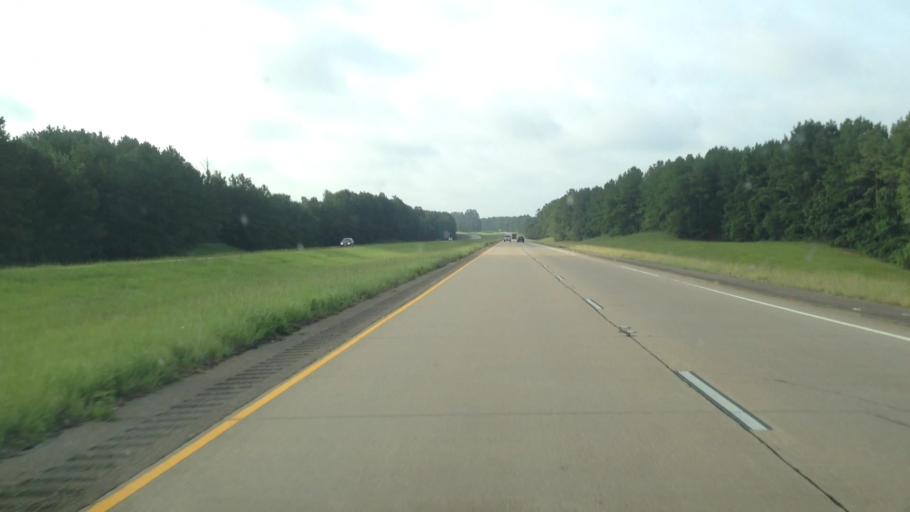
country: US
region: Louisiana
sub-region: Rapides Parish
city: Lecompte
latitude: 31.0473
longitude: -92.4200
